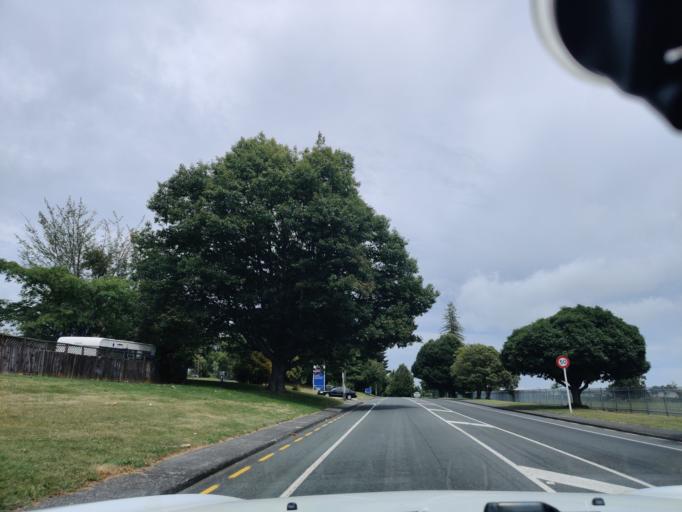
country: NZ
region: Waikato
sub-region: South Waikato District
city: Tokoroa
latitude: -38.2292
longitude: 175.8620
